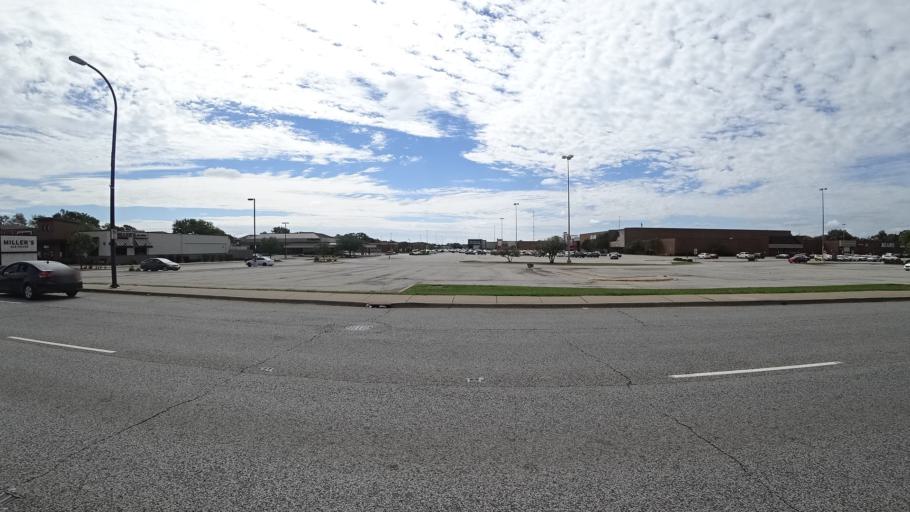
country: US
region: Illinois
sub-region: Cook County
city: Burbank
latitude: 41.7195
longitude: -87.7812
